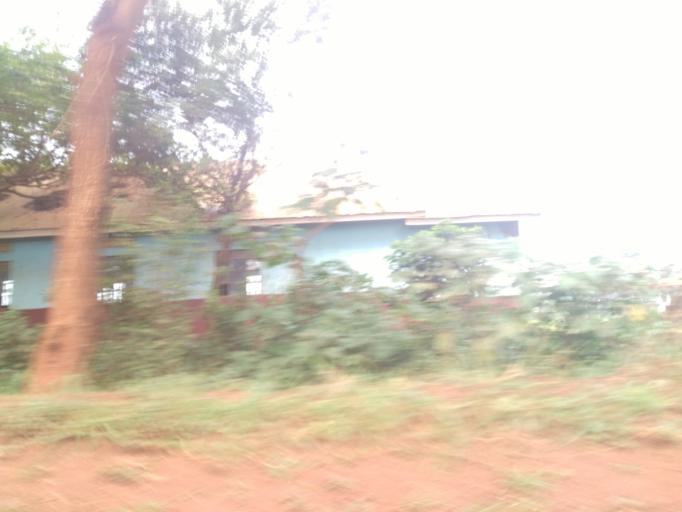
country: UG
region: Central Region
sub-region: Buikwe District
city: Njeru
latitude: 0.4224
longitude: 33.1878
